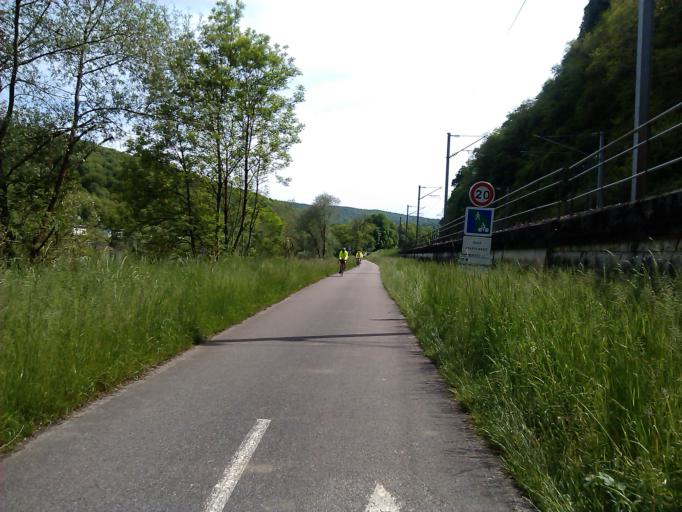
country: FR
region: Franche-Comte
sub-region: Departement du Doubs
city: Boussieres
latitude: 47.1585
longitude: 5.8826
